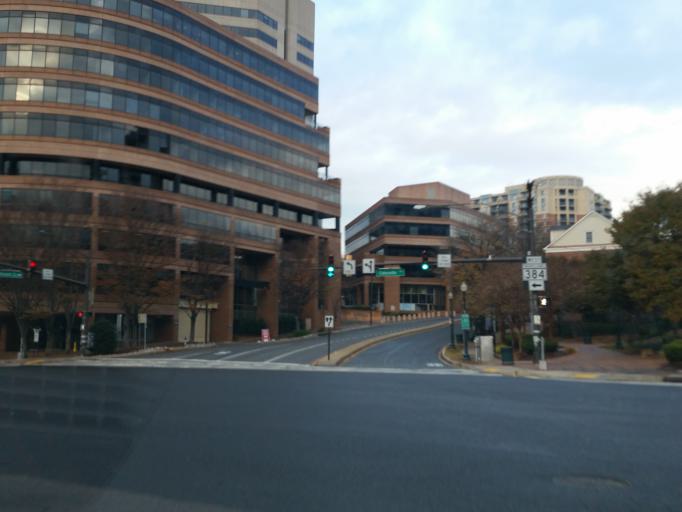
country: US
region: Maryland
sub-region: Montgomery County
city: Silver Spring
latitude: 38.9948
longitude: -77.0300
